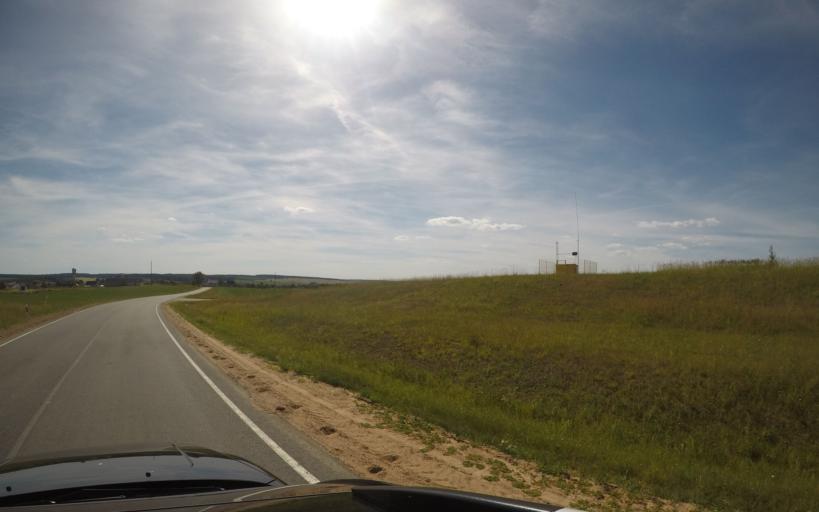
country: BY
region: Grodnenskaya
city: Hal'shany
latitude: 54.2636
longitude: 26.0244
